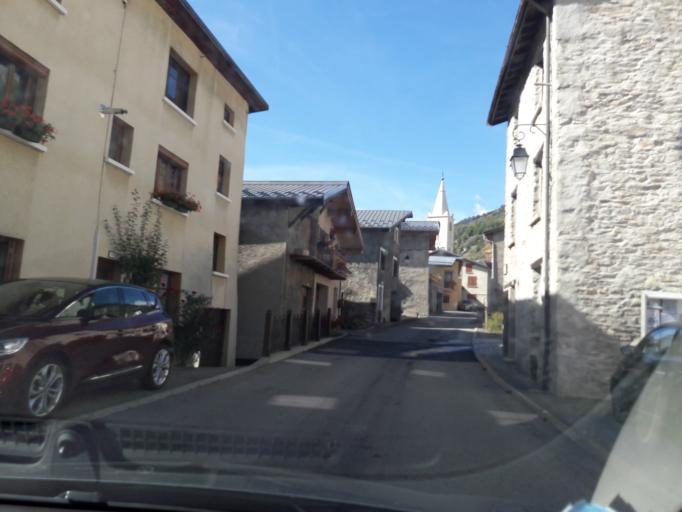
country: FR
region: Rhone-Alpes
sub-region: Departement de la Savoie
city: Modane
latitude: 45.2137
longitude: 6.6988
